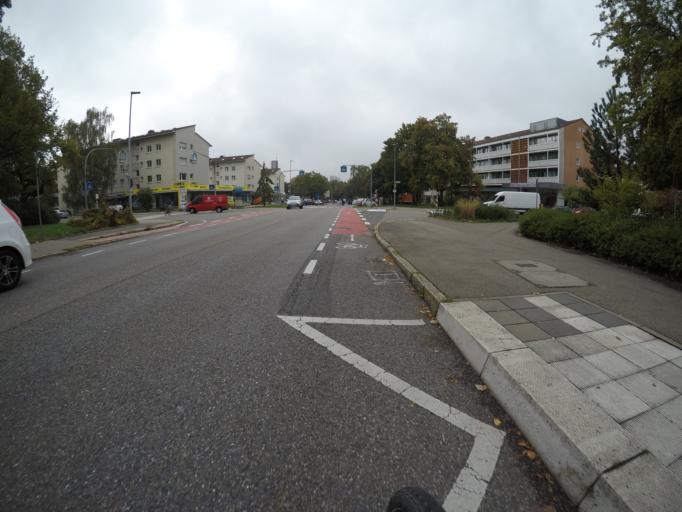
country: DE
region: Baden-Wuerttemberg
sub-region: Regierungsbezirk Stuttgart
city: Boeblingen
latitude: 48.6819
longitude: 9.0054
